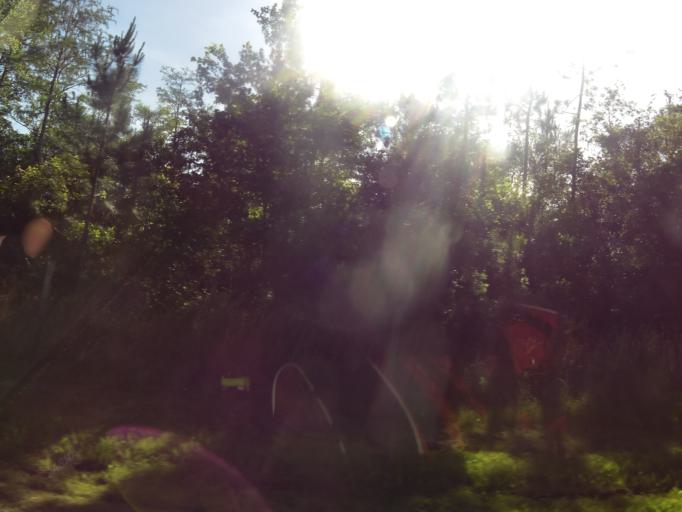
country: US
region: Florida
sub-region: Nassau County
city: Callahan
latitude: 30.5527
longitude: -81.7925
